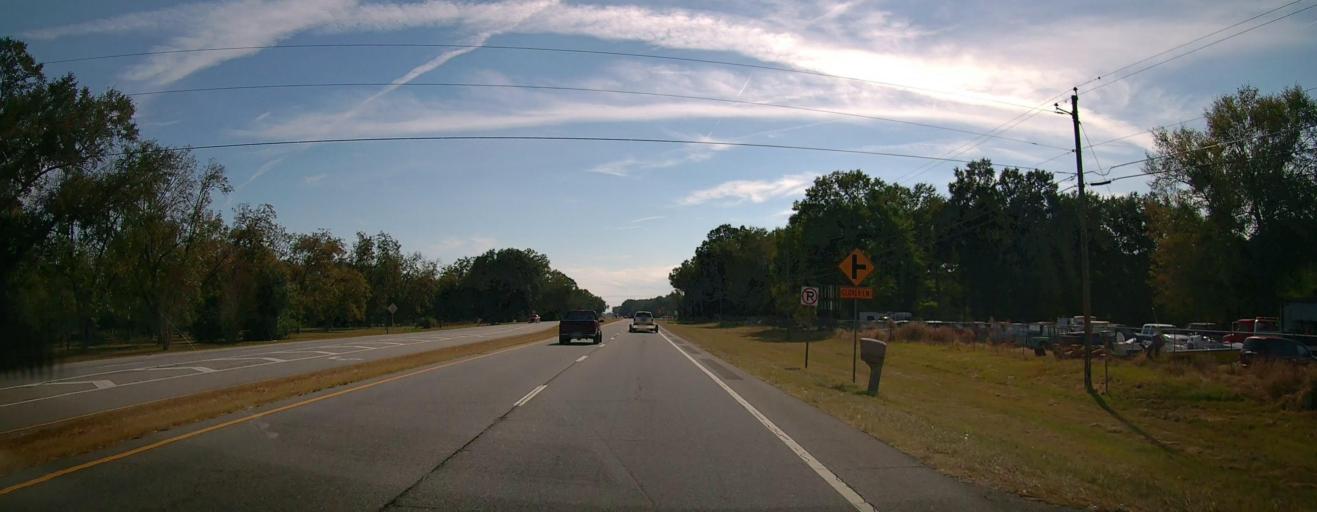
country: US
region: Georgia
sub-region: Dougherty County
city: Putney
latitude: 31.4751
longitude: -84.1175
